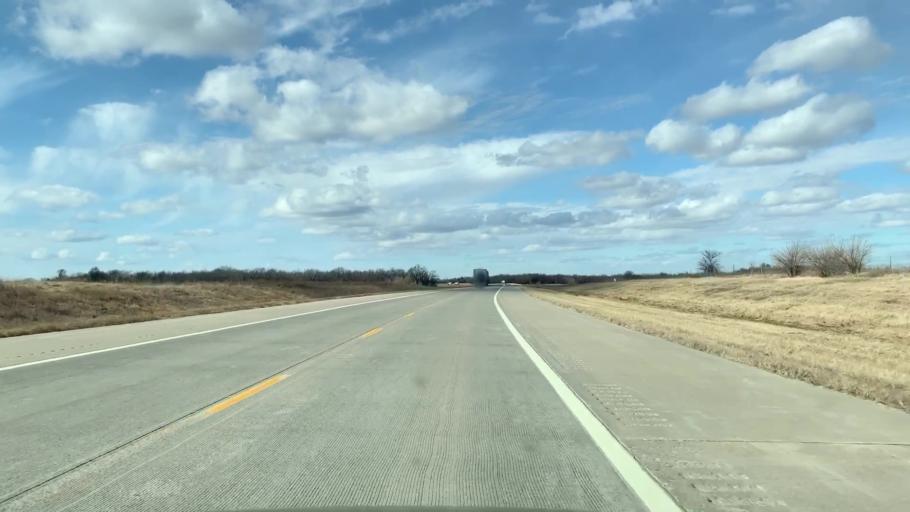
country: US
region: Kansas
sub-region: Labette County
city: Parsons
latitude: 37.3540
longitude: -95.2120
